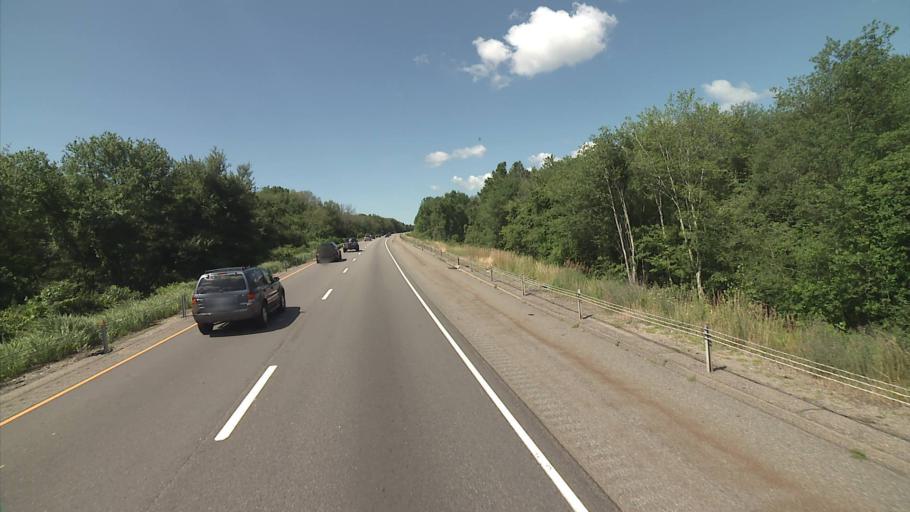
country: US
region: Connecticut
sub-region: New London County
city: Pawcatuck
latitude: 41.3922
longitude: -71.8747
